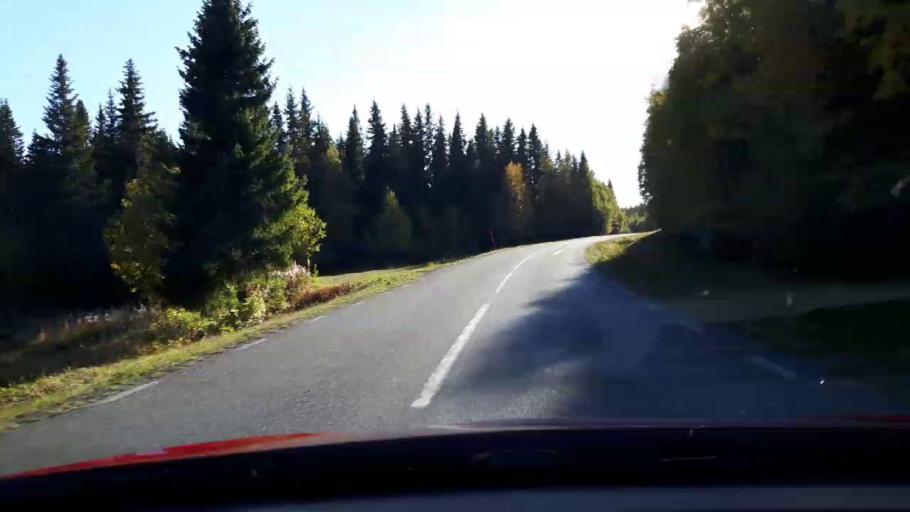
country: SE
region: Jaemtland
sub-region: OEstersunds Kommun
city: Lit
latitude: 63.8279
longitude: 14.8665
